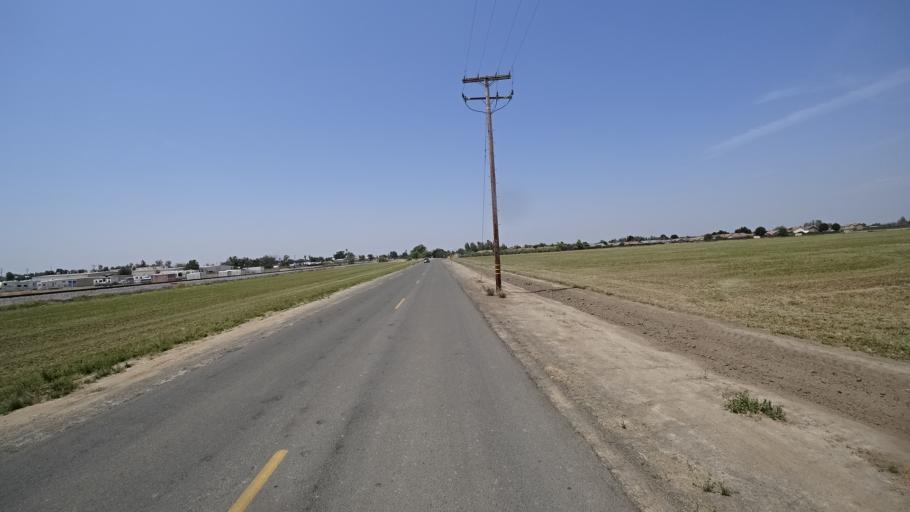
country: US
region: California
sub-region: Kings County
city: Armona
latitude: 36.3177
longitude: -119.6958
